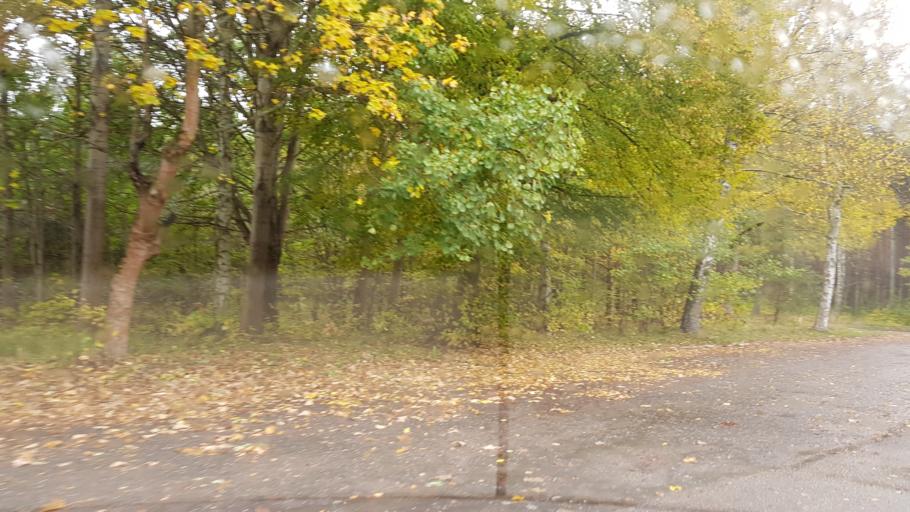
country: PL
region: West Pomeranian Voivodeship
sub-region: Powiat walecki
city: Walcz
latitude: 53.3839
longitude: 16.4863
